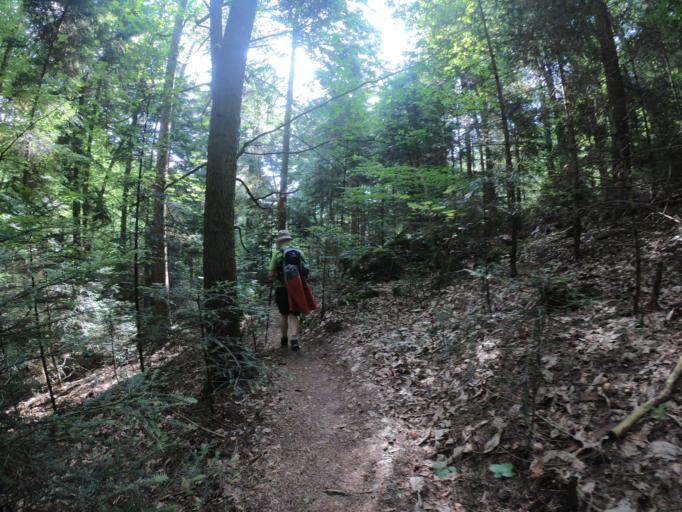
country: DE
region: Rheinland-Pfalz
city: Gleiszellen-Gleishorbach
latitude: 49.1320
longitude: 7.9875
